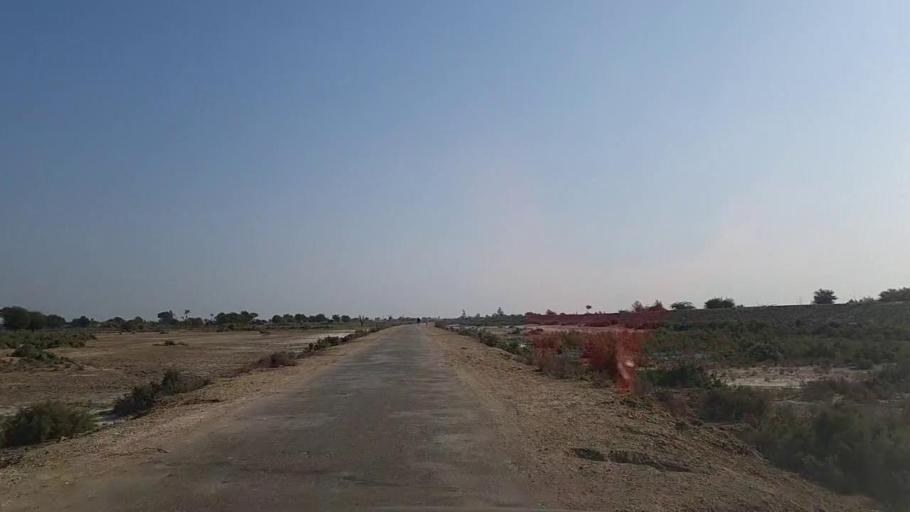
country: PK
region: Sindh
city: Sanghar
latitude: 25.9627
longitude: 69.0377
